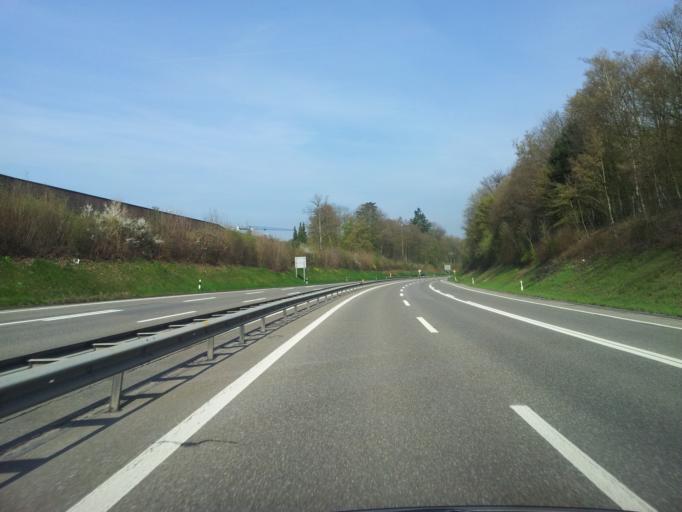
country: CH
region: Aargau
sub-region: Bezirk Aarau
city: Buchs
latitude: 47.3897
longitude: 8.0893
